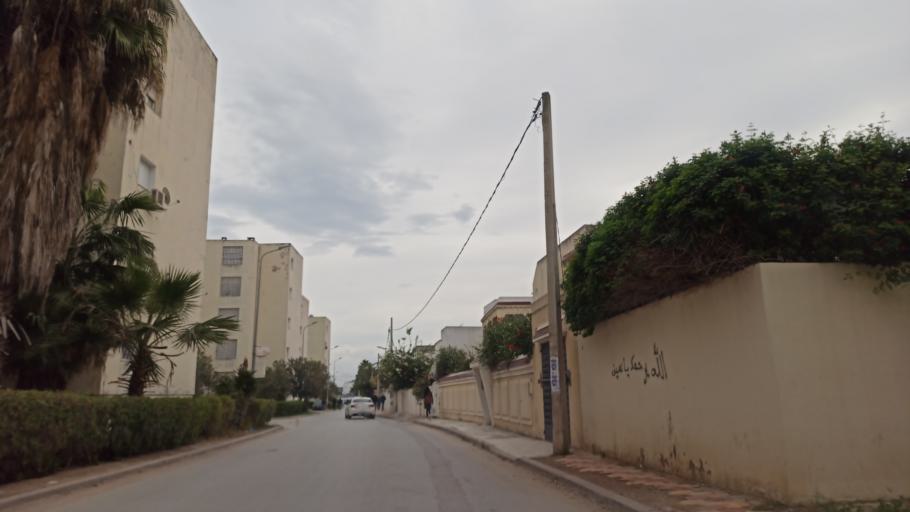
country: TN
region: Tunis
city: La Goulette
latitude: 36.8562
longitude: 10.2676
